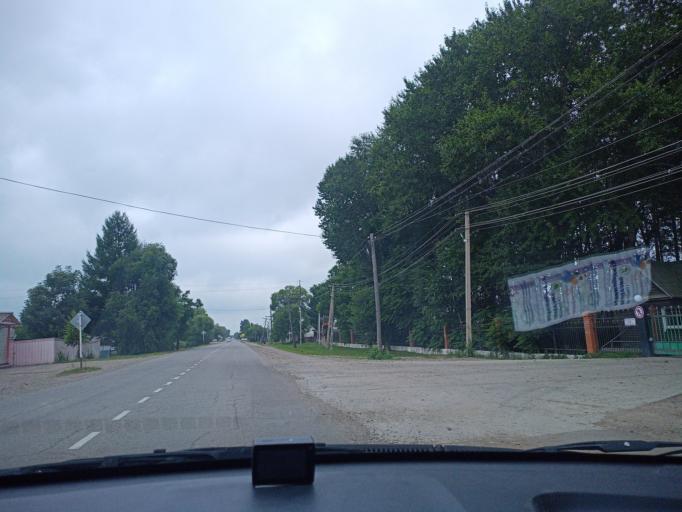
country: RU
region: Primorskiy
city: Novopokrovka
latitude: 45.8979
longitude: 134.8838
